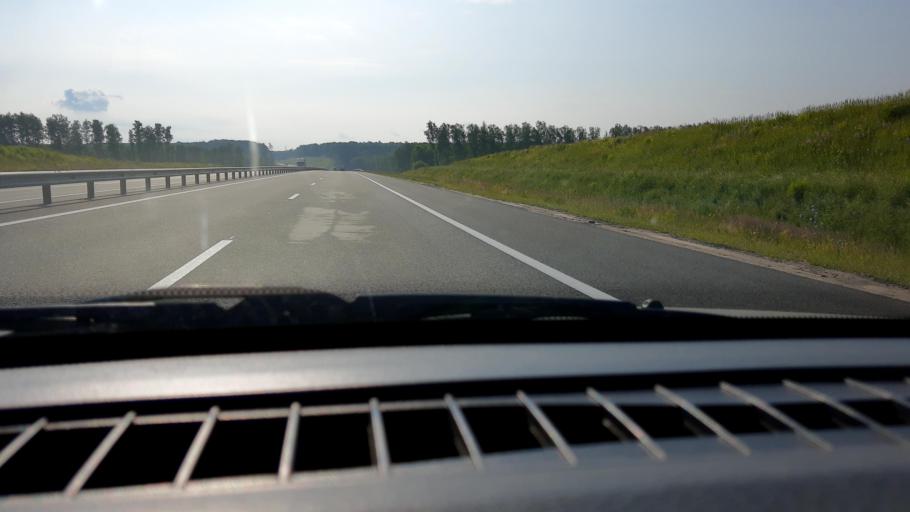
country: RU
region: Nizjnij Novgorod
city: Afonino
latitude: 56.1037
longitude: 44.0077
